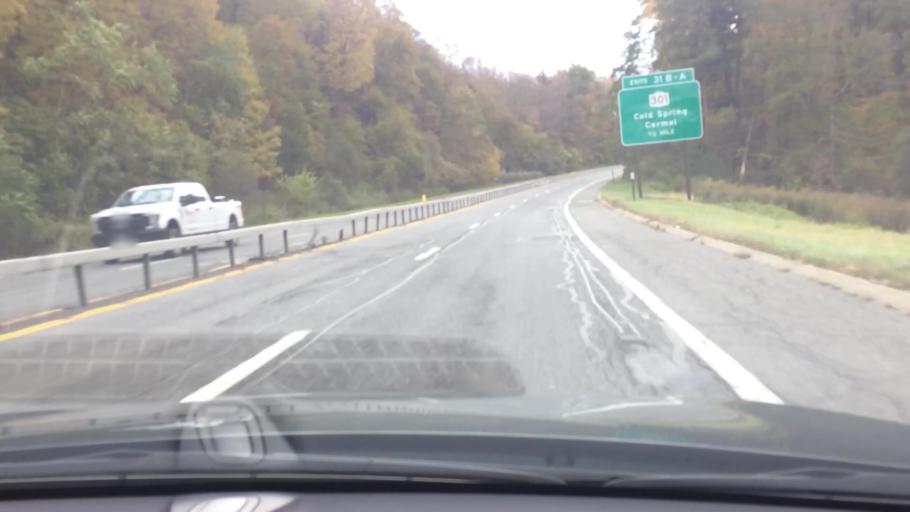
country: US
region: New York
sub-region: Dutchess County
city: Brinckerhoff
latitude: 41.4733
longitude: -73.8189
